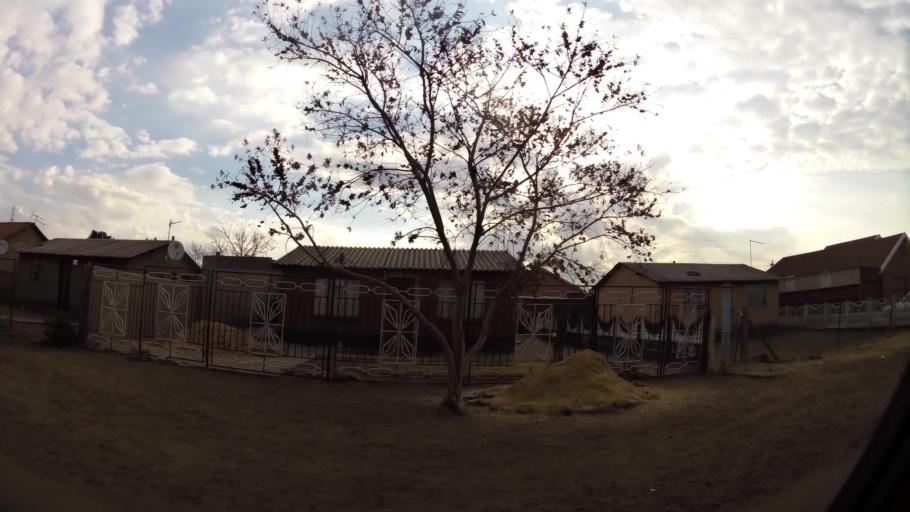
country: ZA
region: Gauteng
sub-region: Sedibeng District Municipality
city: Vanderbijlpark
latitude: -26.6904
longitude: 27.8799
